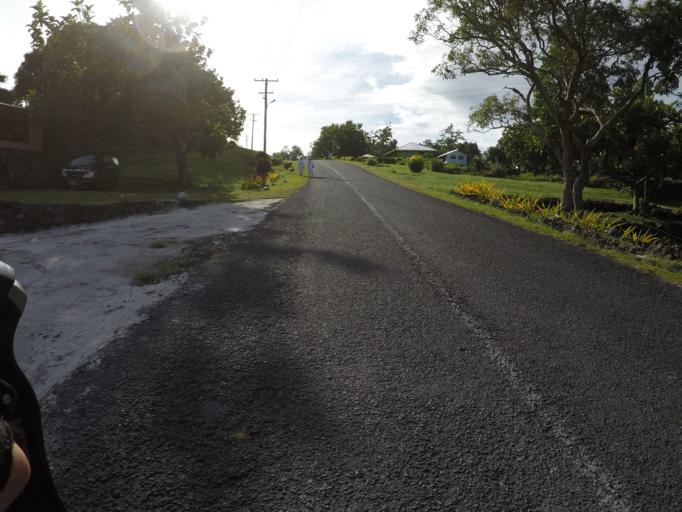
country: WS
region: Vaisigano
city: Asau
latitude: -13.6490
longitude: -172.6610
